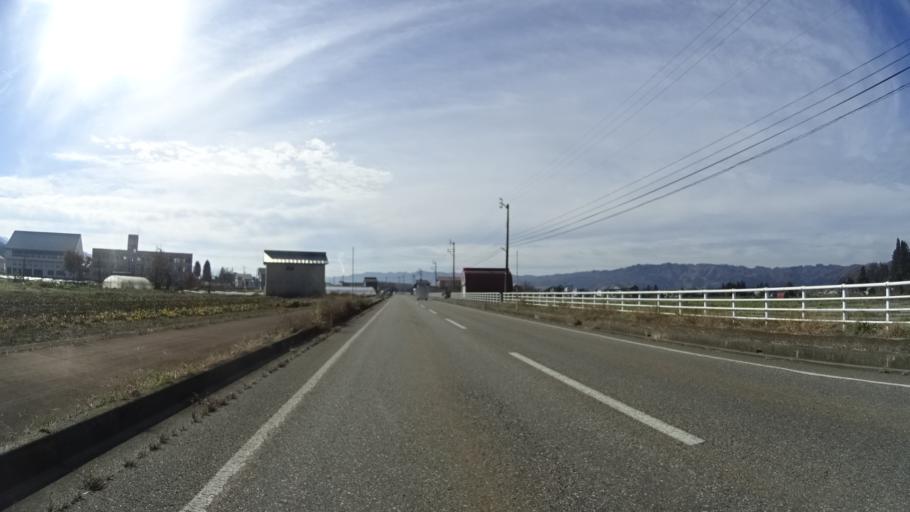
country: JP
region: Niigata
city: Muikamachi
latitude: 37.1788
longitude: 138.9735
